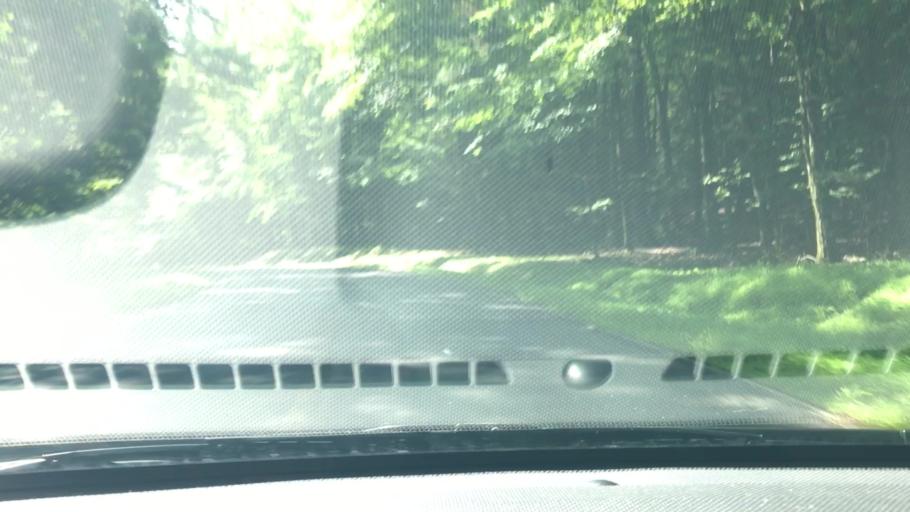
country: US
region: New York
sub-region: Ulster County
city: Shokan
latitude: 41.9327
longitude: -74.2455
